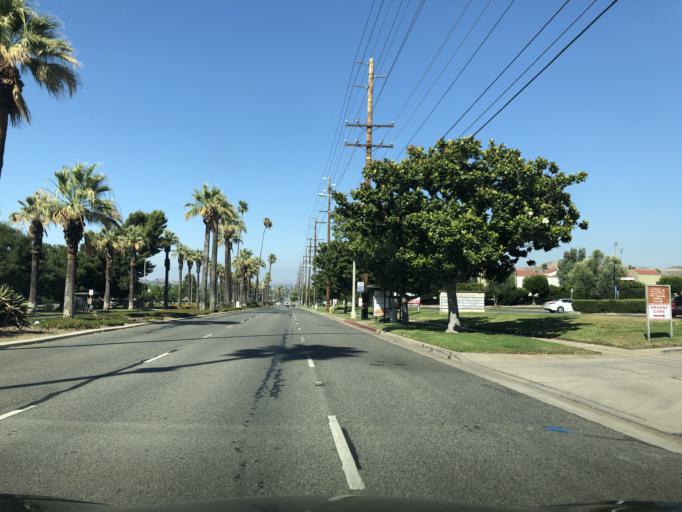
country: US
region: California
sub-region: Riverside County
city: Corona
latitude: 33.8595
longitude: -117.5533
